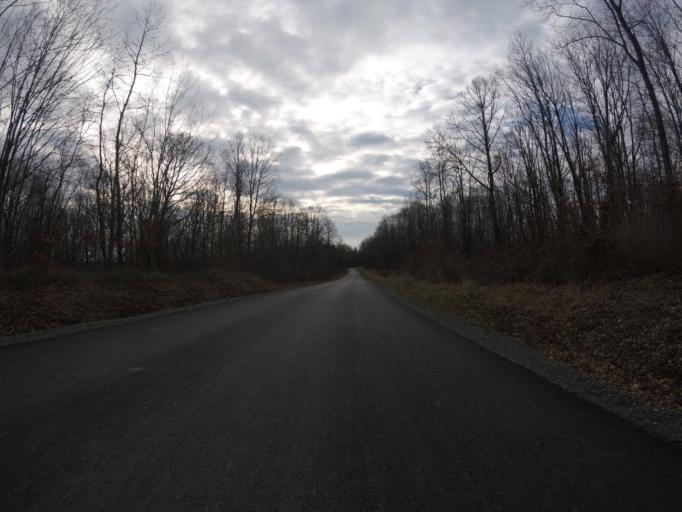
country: HR
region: Sisacko-Moslavacka
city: Glina
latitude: 45.4970
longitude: 16.0453
